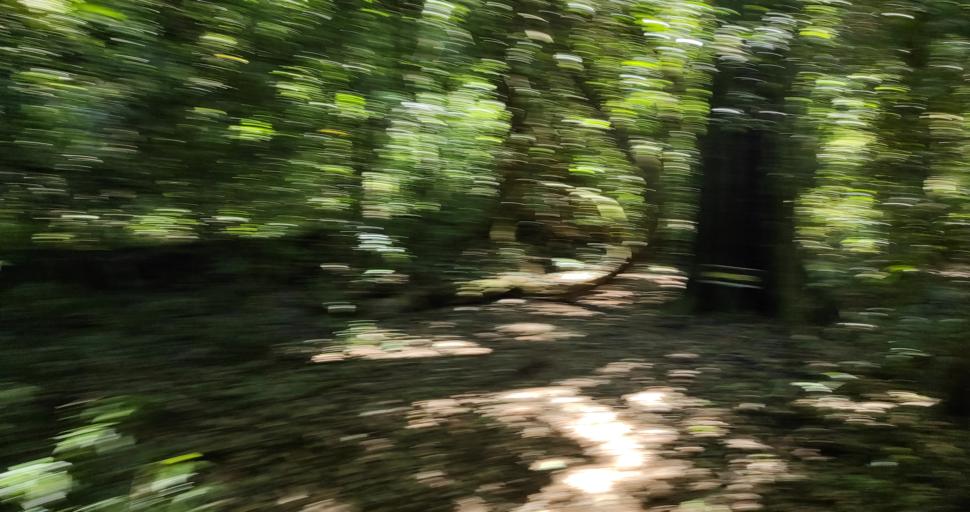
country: BR
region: Rio Grande do Sul
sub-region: Tres Passos
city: Tres Passos
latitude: -27.1482
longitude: -53.8981
